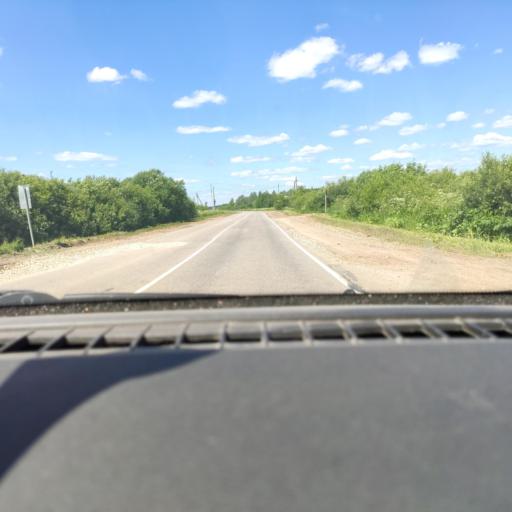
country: RU
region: Perm
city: Chaykovskaya
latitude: 58.0874
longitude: 55.6128
